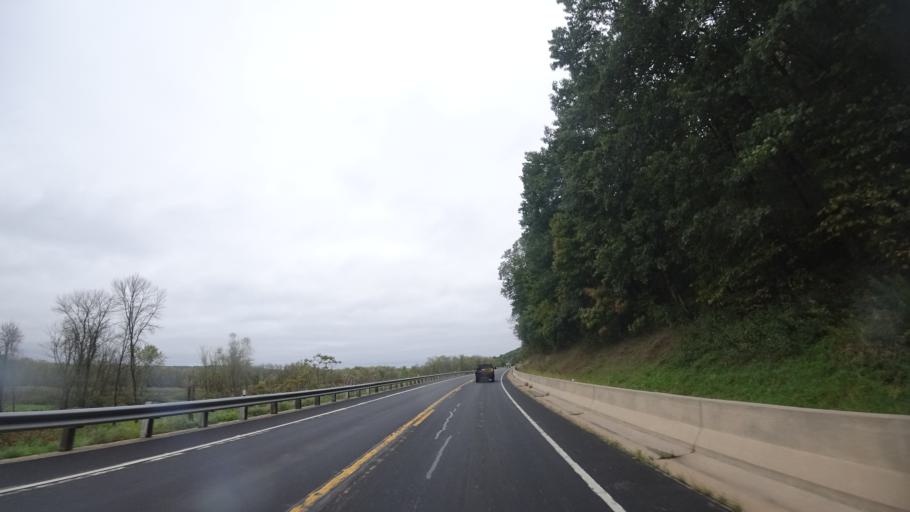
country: US
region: Wisconsin
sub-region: Grant County
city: Boscobel
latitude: 43.1236
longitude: -90.7736
